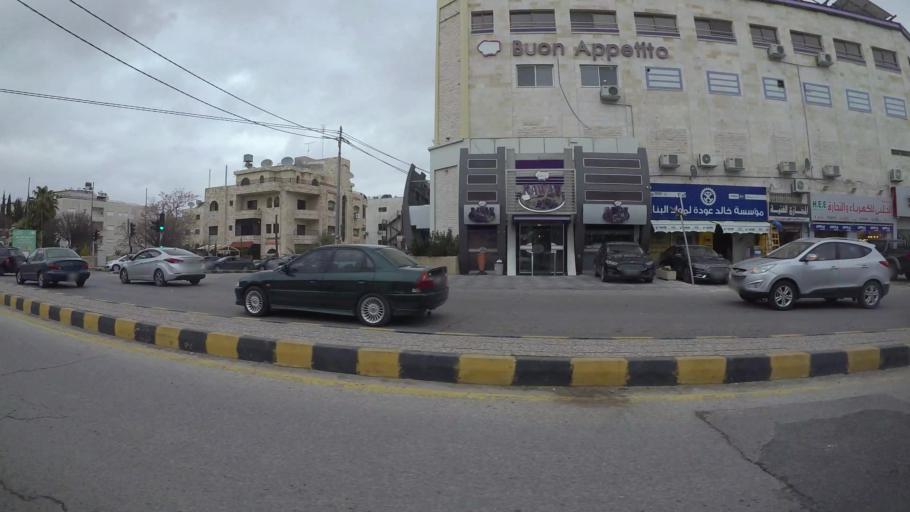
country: JO
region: Amman
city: Wadi as Sir
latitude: 31.9795
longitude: 35.8491
